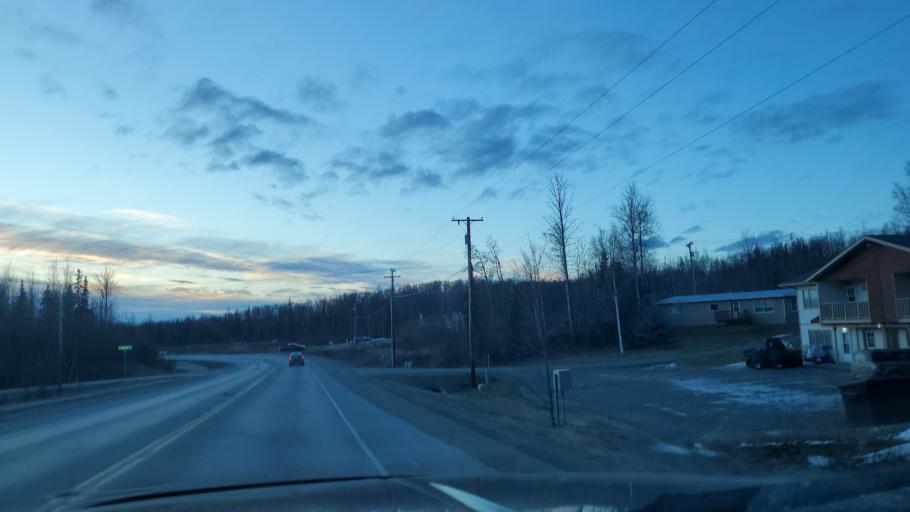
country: US
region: Alaska
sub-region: Matanuska-Susitna Borough
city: Wasilla
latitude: 61.5946
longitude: -149.4336
